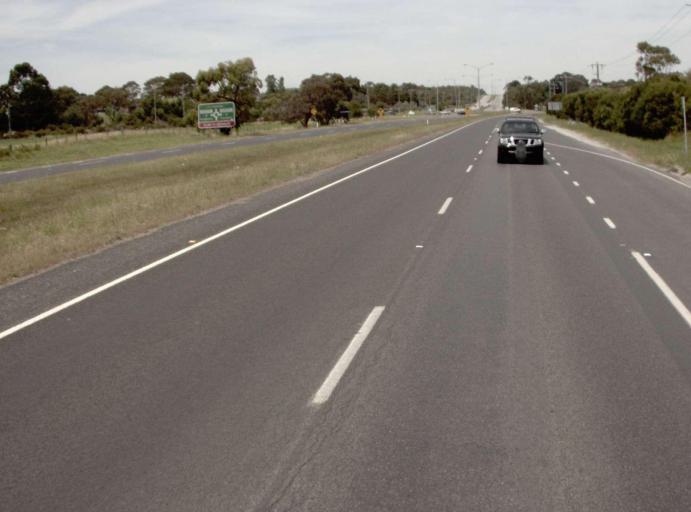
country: AU
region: Victoria
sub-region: Casey
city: Cranbourne South
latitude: -38.1311
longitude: 145.2286
